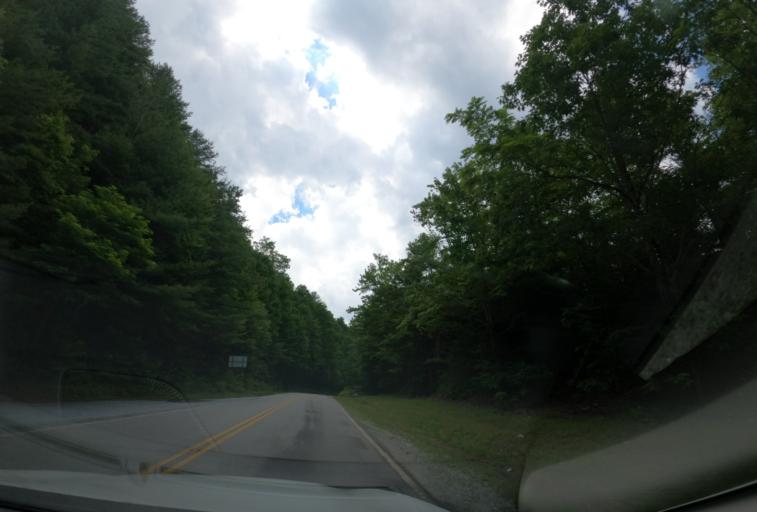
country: US
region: South Carolina
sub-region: Oconee County
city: Walhalla
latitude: 35.0334
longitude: -83.0186
